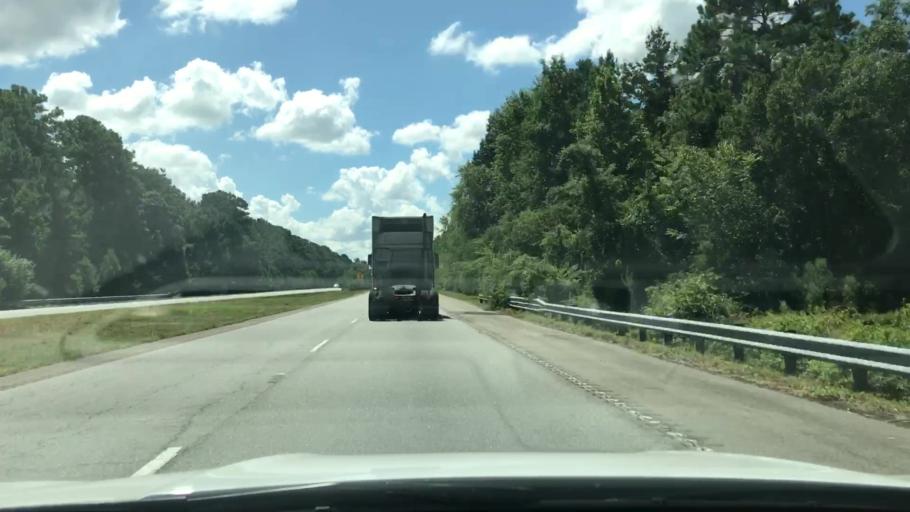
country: US
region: South Carolina
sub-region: Berkeley County
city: Hanahan
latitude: 32.9372
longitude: -79.9978
